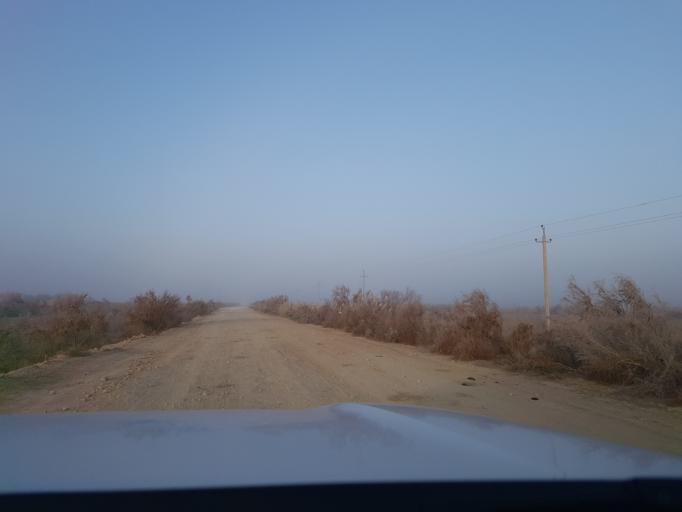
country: TM
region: Dasoguz
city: Koeneuergench
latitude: 41.8455
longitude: 58.4113
